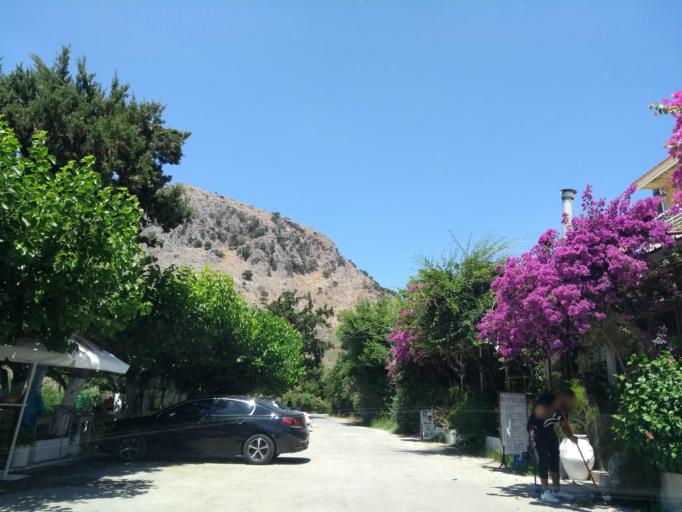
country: GR
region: Crete
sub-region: Nomos Chanias
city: Georgioupolis
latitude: 35.3349
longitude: 24.2769
